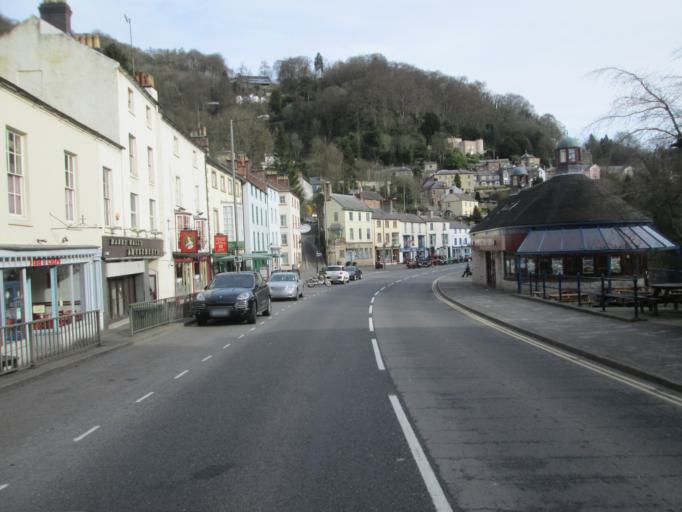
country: GB
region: England
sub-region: Derbyshire
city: Cromford
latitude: 53.1199
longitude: -1.5635
